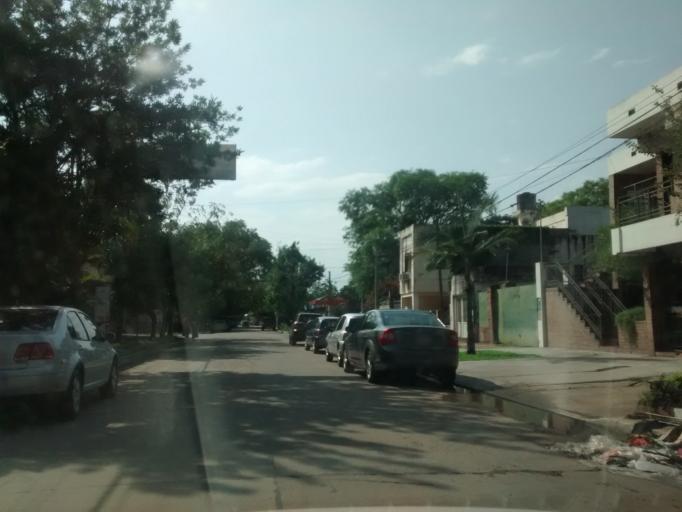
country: AR
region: Chaco
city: Resistencia
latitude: -27.4602
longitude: -58.9780
